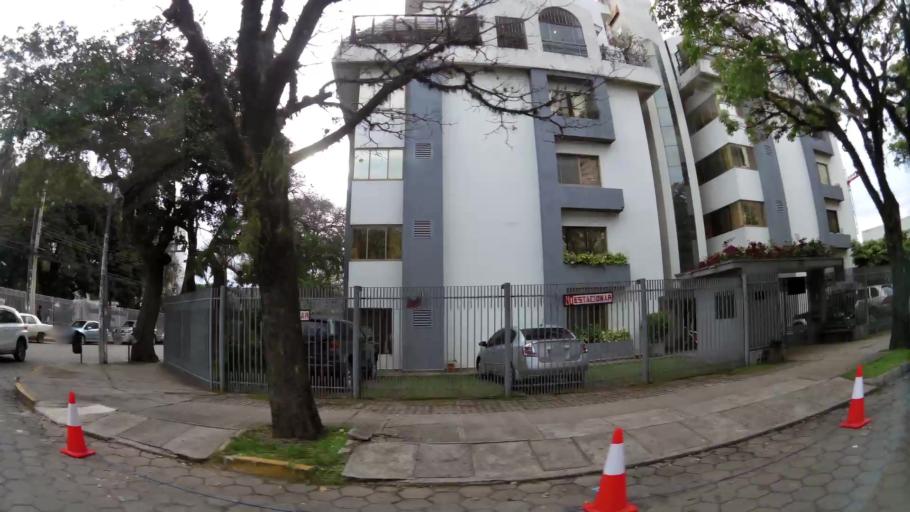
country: BO
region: Santa Cruz
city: Santa Cruz de la Sierra
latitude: -17.7909
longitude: -63.1798
